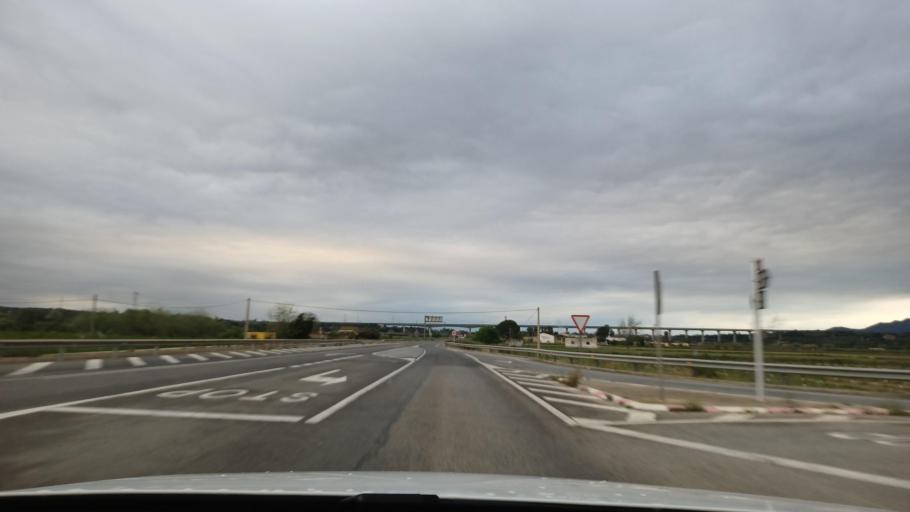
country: ES
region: Catalonia
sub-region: Provincia de Tarragona
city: Amposta
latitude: 40.7421
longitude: 0.5635
